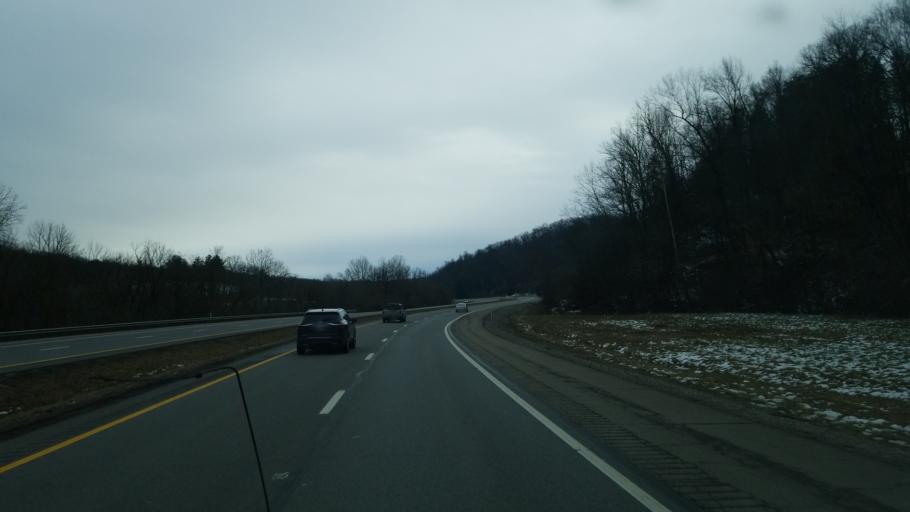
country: US
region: West Virginia
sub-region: Wood County
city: Mineral Wells
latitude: 39.1372
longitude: -81.5489
